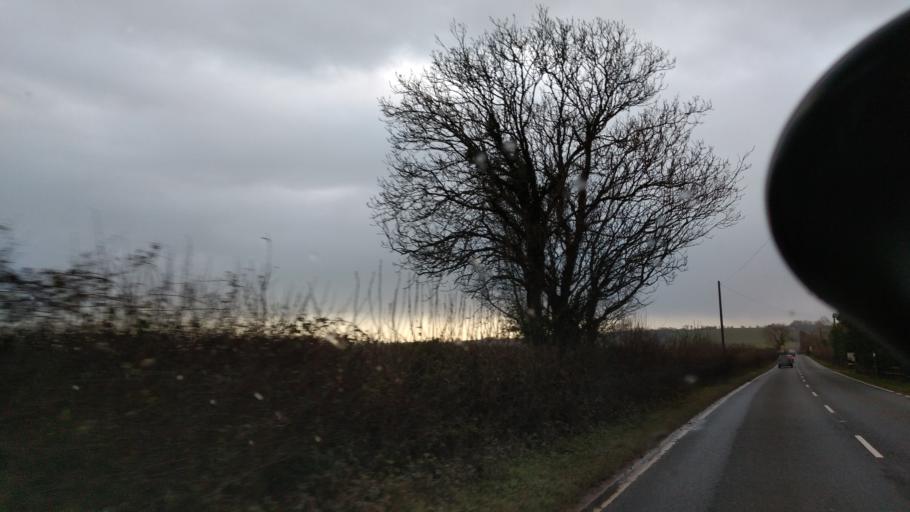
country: GB
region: England
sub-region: Somerset
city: Shepton Mallet
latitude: 51.1606
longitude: -2.5409
